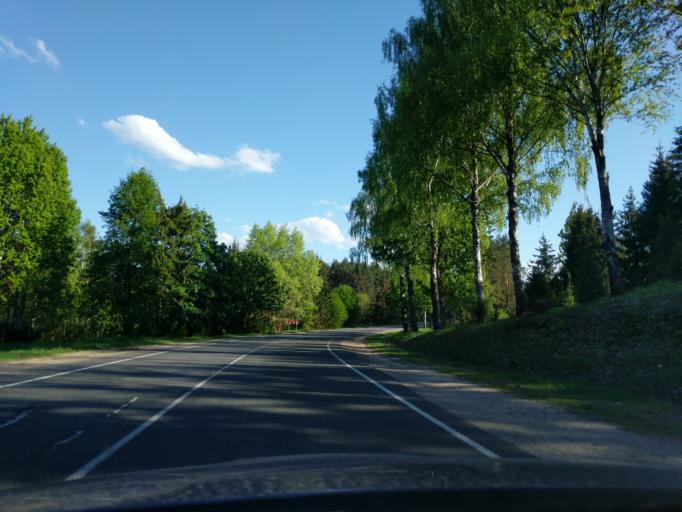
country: BY
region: Minsk
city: Myadzyel
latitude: 54.8540
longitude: 26.9244
